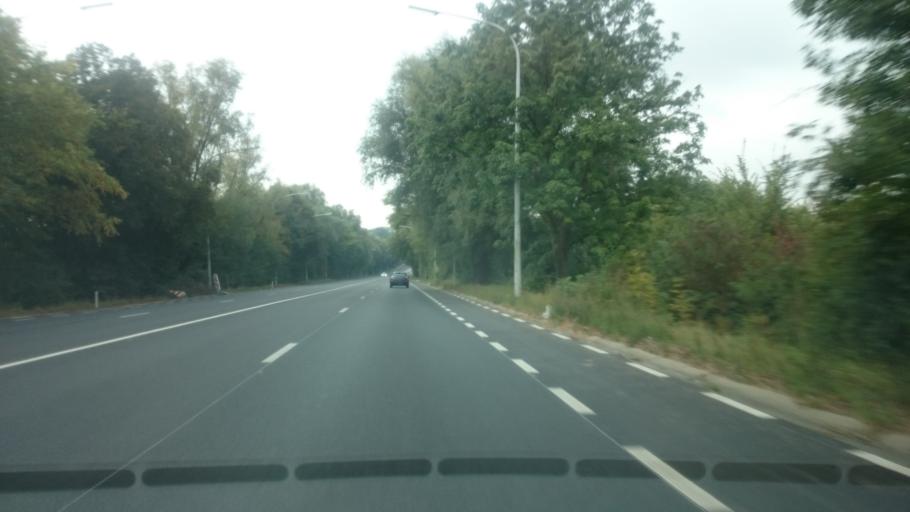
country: BE
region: Wallonia
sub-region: Province de Namur
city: Namur
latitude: 50.4752
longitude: 4.8073
